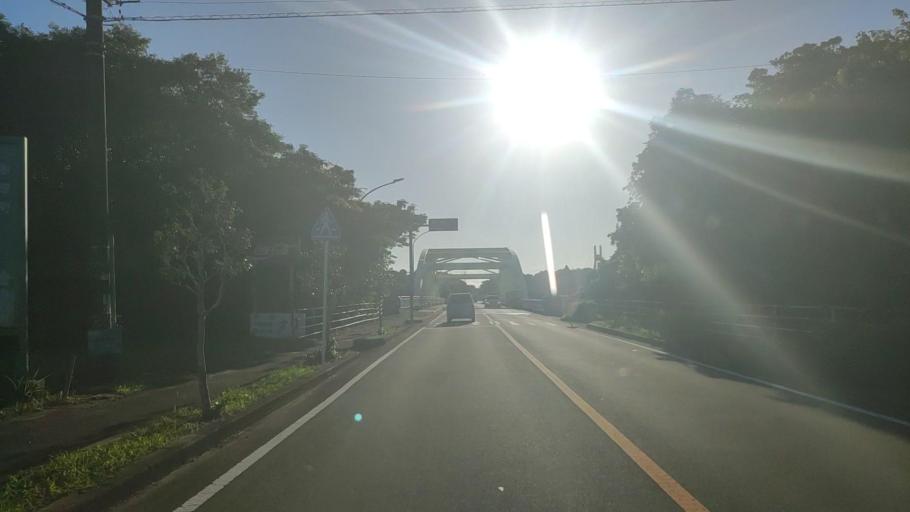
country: JP
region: Mie
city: Toba
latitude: 34.2601
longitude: 136.8348
